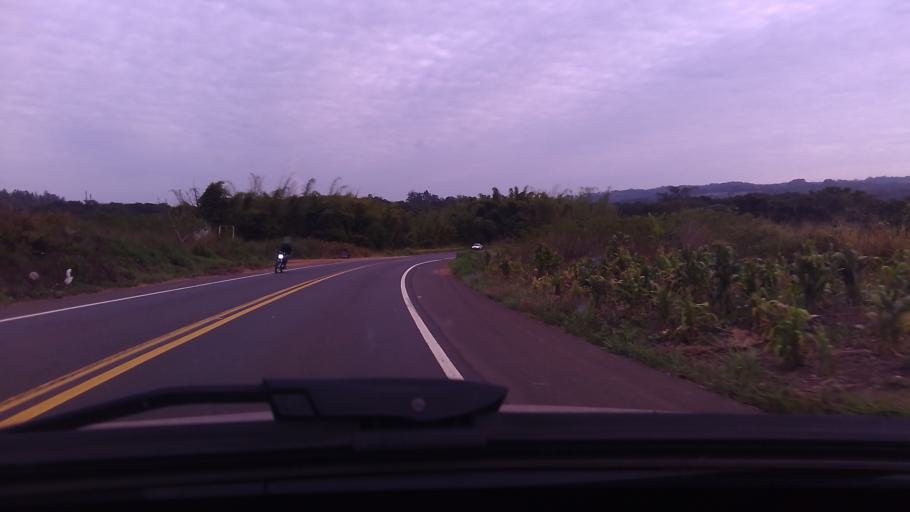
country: BR
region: Goias
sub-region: Mineiros
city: Mineiros
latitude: -17.5846
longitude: -52.5023
